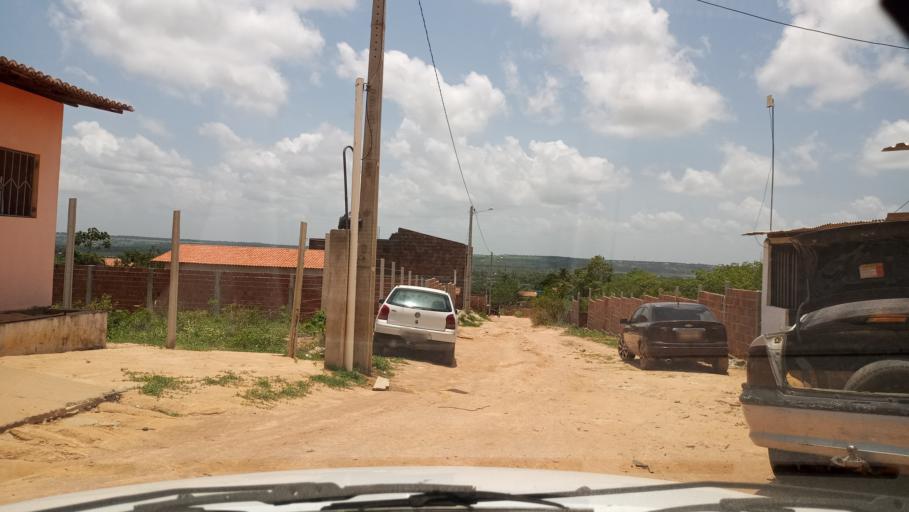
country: BR
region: Rio Grande do Norte
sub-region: Ares
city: Ares
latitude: -6.2344
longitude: -35.1456
